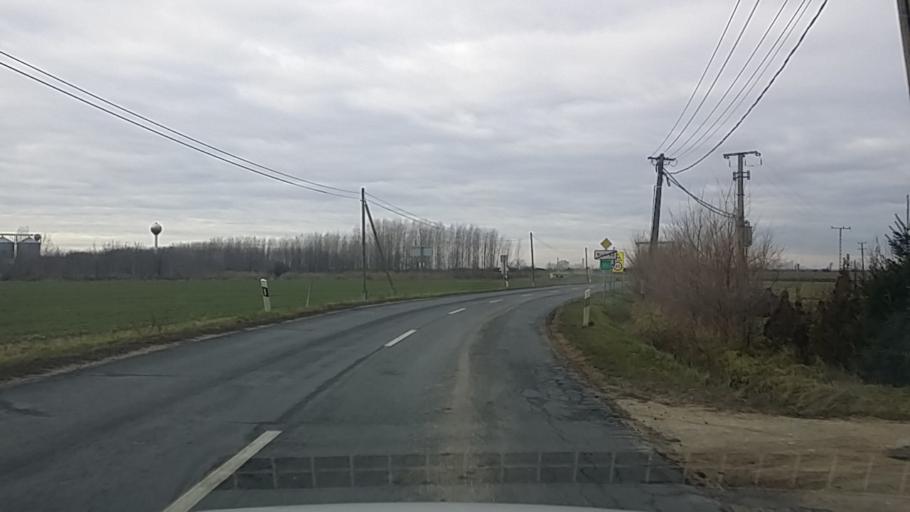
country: HU
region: Veszprem
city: Papa
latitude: 47.2808
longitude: 17.3534
